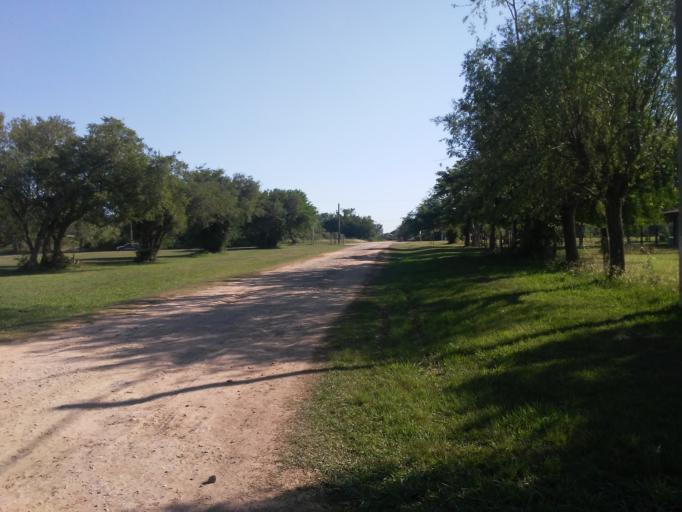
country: AR
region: Buenos Aires
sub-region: Partido de San Pedro
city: San Pedro
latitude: -33.5962
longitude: -59.8146
